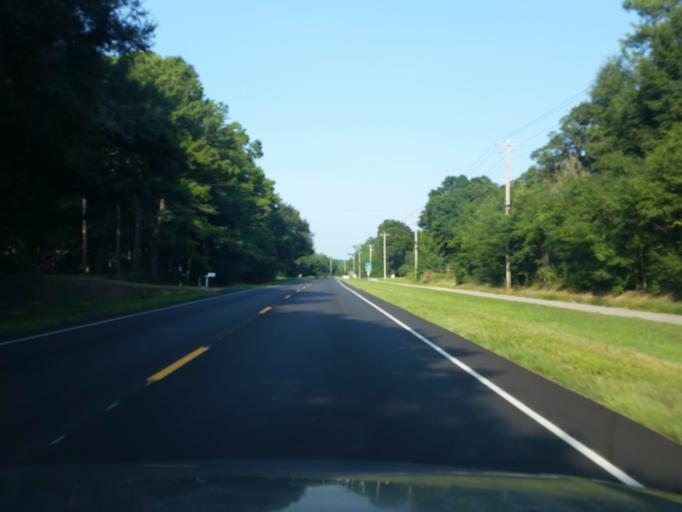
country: US
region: Alabama
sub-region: Baldwin County
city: Point Clear
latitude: 30.4199
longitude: -87.8385
